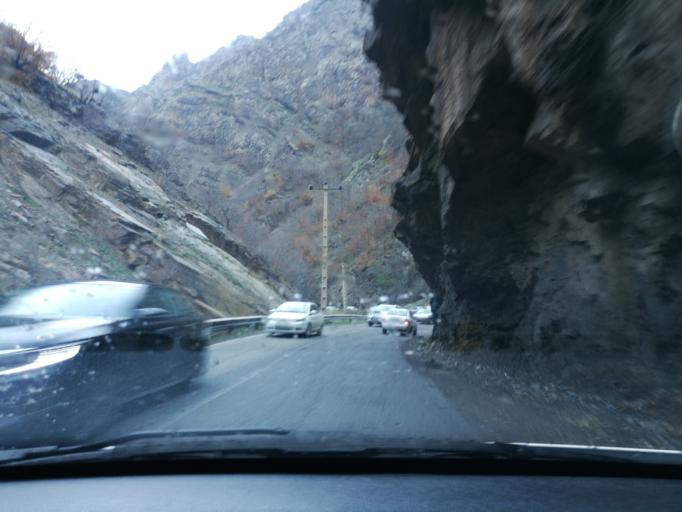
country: IR
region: Mazandaran
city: Chalus
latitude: 36.2844
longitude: 51.2424
